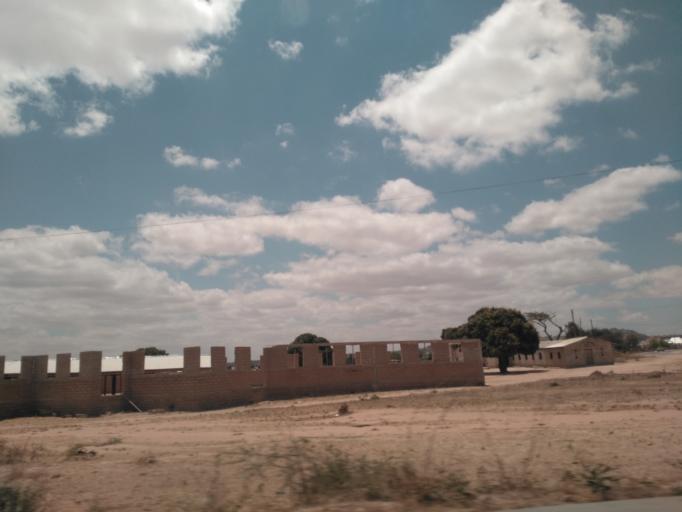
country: TZ
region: Dodoma
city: Kisasa
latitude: -6.1704
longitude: 35.7930
